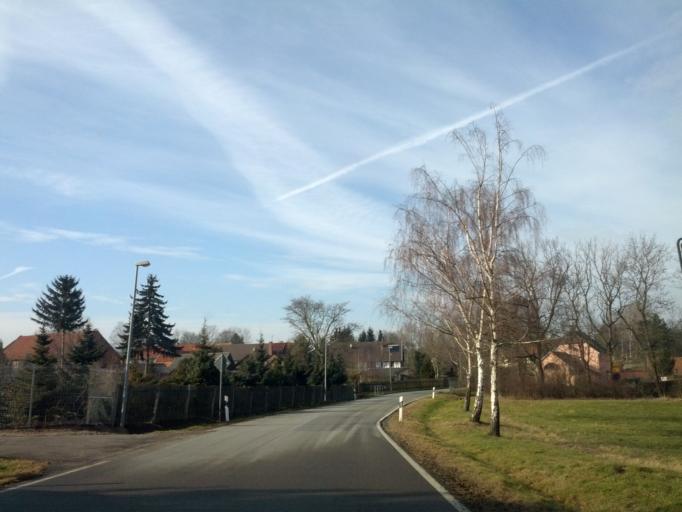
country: DE
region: Thuringia
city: Schonstedt
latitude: 51.0954
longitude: 10.5535
